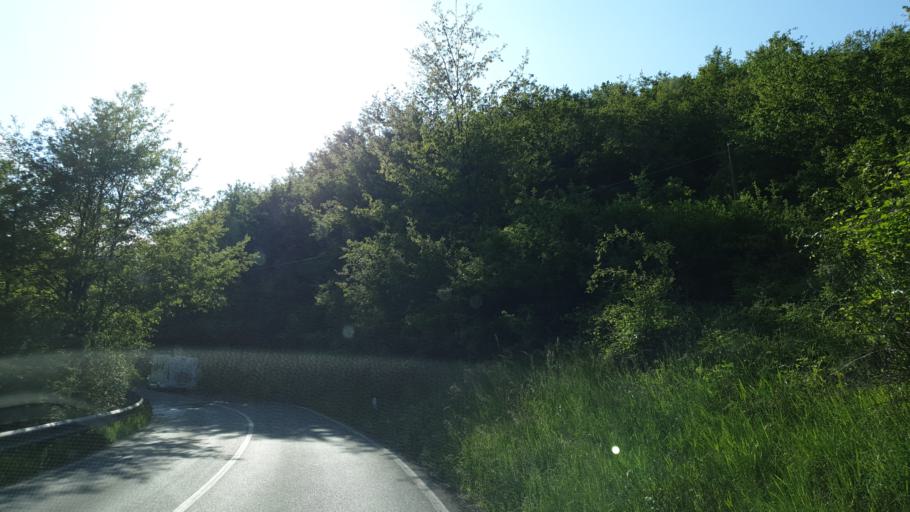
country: IT
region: Tuscany
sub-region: Province of Arezzo
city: Stia
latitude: 43.7814
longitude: 11.6703
